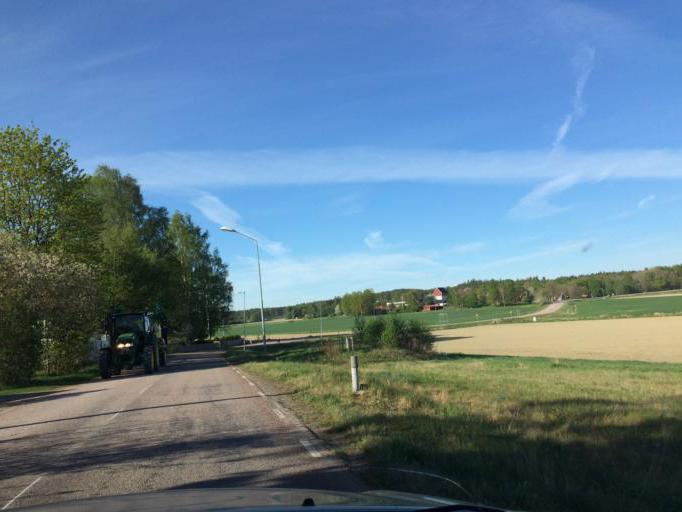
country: SE
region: Soedermanland
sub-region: Eskilstuna Kommun
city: Kvicksund
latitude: 59.4240
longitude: 16.3384
